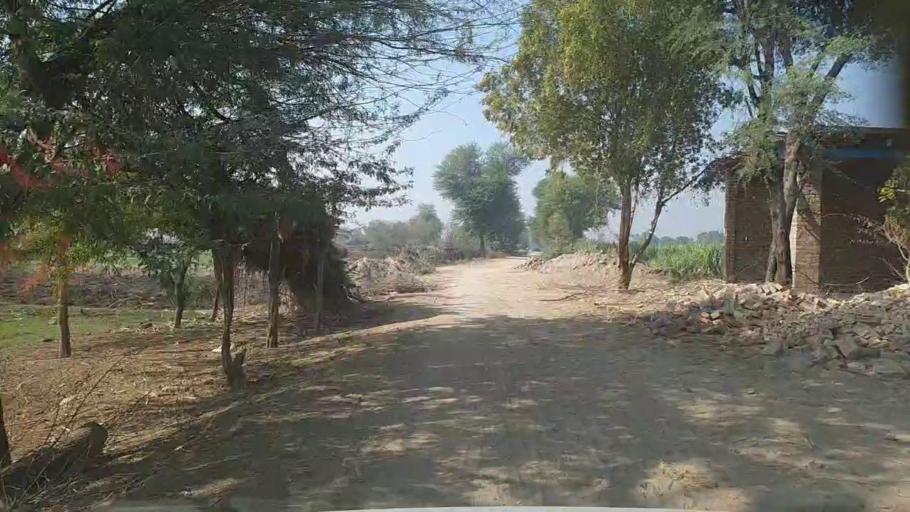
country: PK
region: Sindh
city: Kandiari
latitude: 26.9943
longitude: 68.4870
